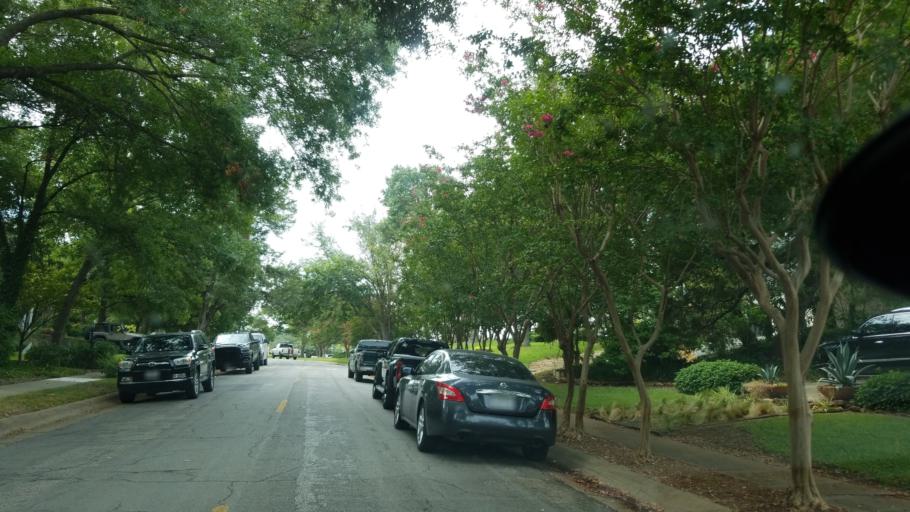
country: US
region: Texas
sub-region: Dallas County
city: Cockrell Hill
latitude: 32.7577
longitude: -96.8467
